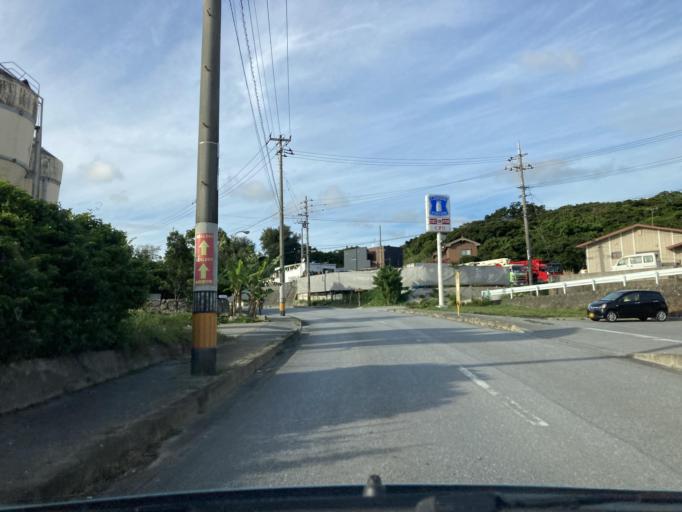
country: JP
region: Okinawa
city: Tomigusuku
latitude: 26.1458
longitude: 127.7451
